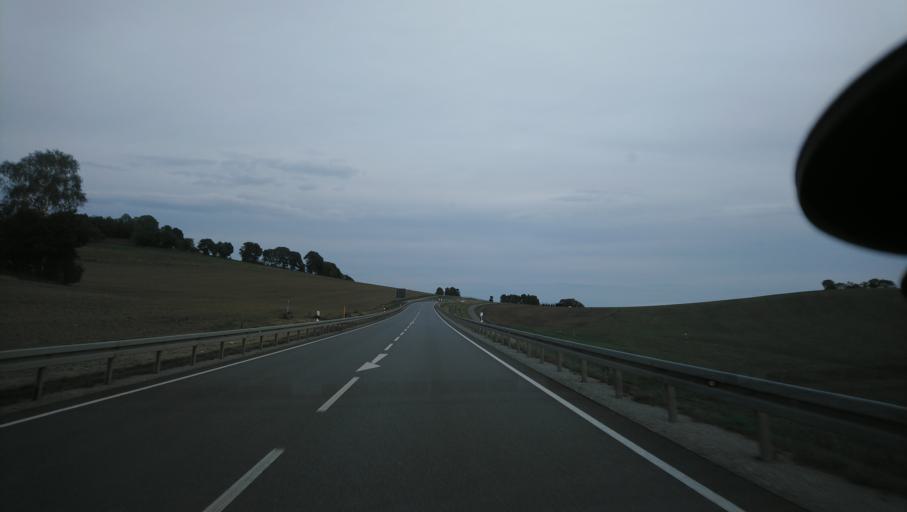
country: DE
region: Saxony
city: Ehrenfriedersdorf
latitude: 50.6267
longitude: 12.9672
